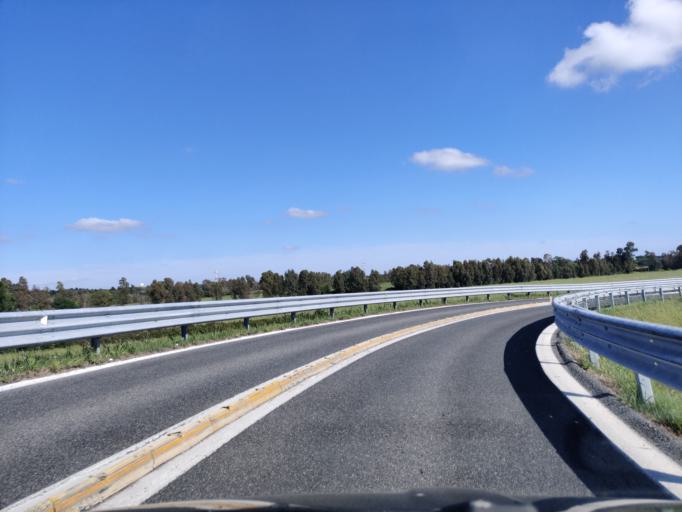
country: IT
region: Latium
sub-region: Citta metropolitana di Roma Capitale
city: Maccarese
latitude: 41.8891
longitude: 12.2307
